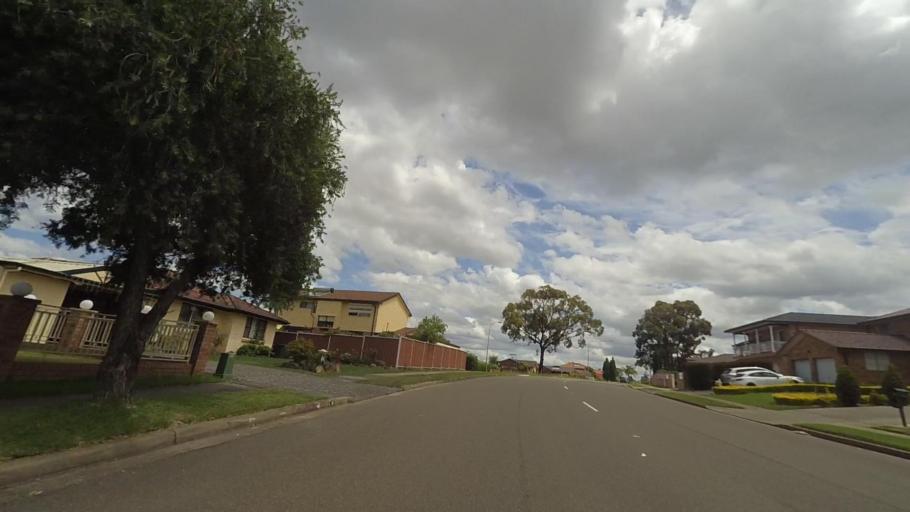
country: AU
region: New South Wales
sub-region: Fairfield
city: Cabramatta West
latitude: -33.8730
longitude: 150.9102
